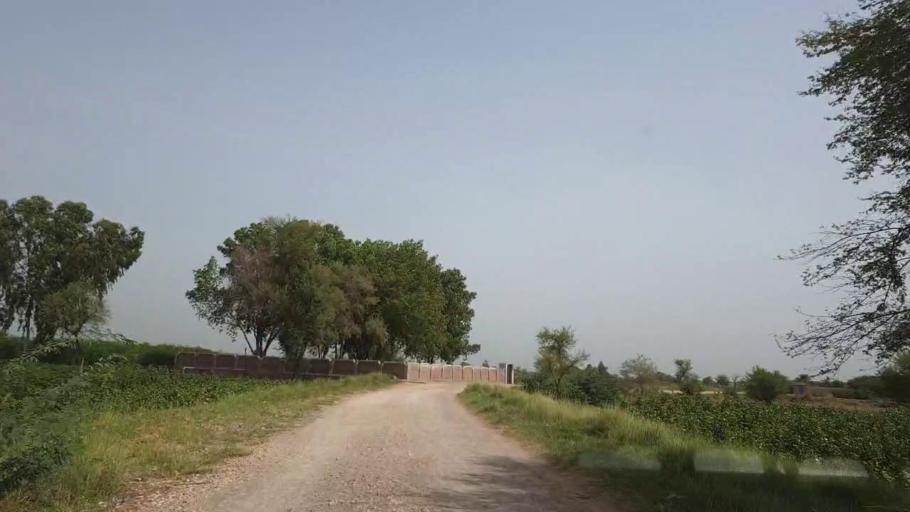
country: PK
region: Sindh
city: Sakrand
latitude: 26.1180
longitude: 68.3688
